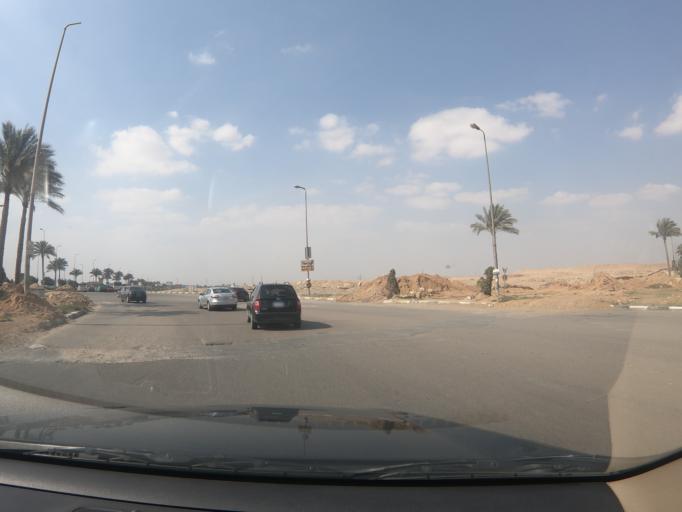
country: EG
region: Muhafazat al Qalyubiyah
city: Al Khankah
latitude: 30.0708
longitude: 31.4749
